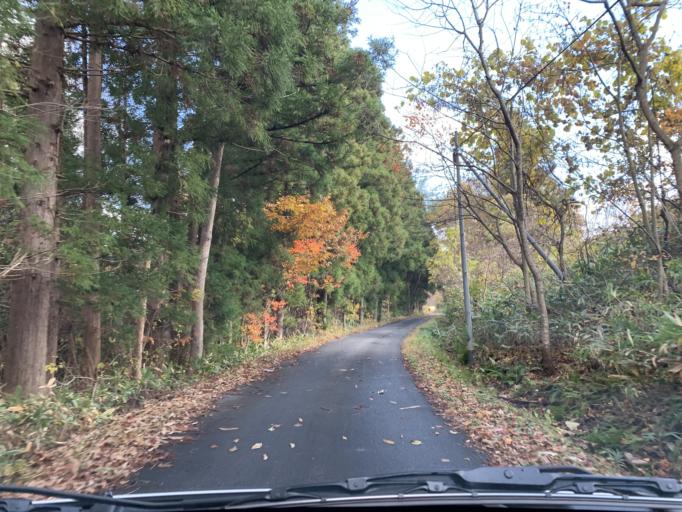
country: JP
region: Iwate
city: Mizusawa
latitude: 39.1030
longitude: 140.9825
